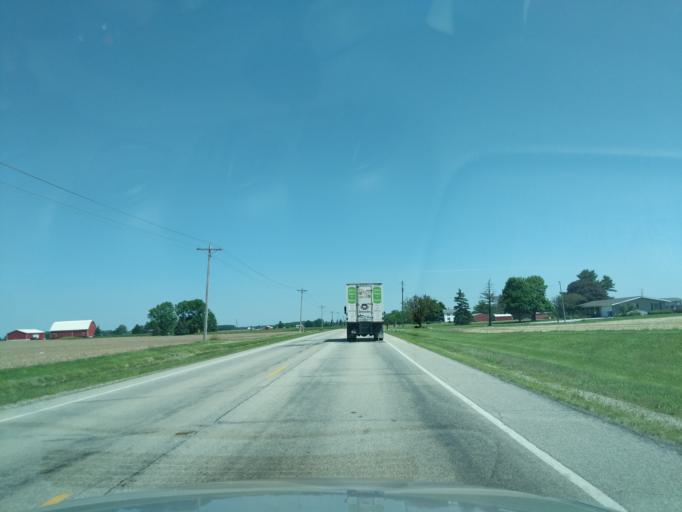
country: US
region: Indiana
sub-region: Whitley County
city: Columbia City
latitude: 41.0398
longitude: -85.4706
